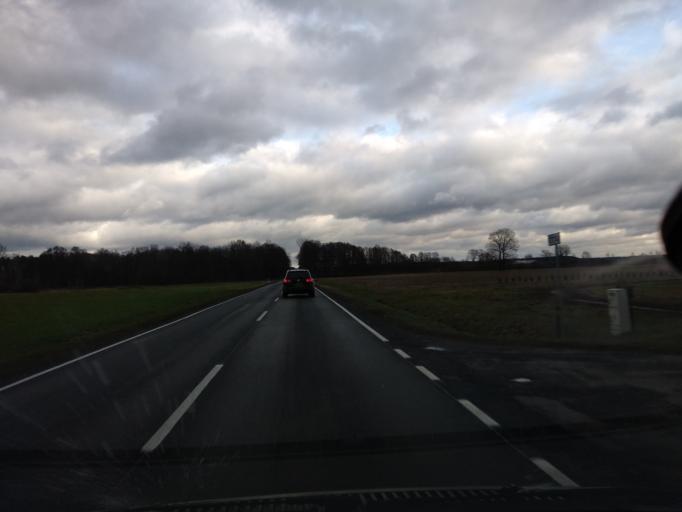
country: PL
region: Greater Poland Voivodeship
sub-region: Powiat ostrowski
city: Jankow Przygodzki
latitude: 51.4864
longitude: 17.7679
